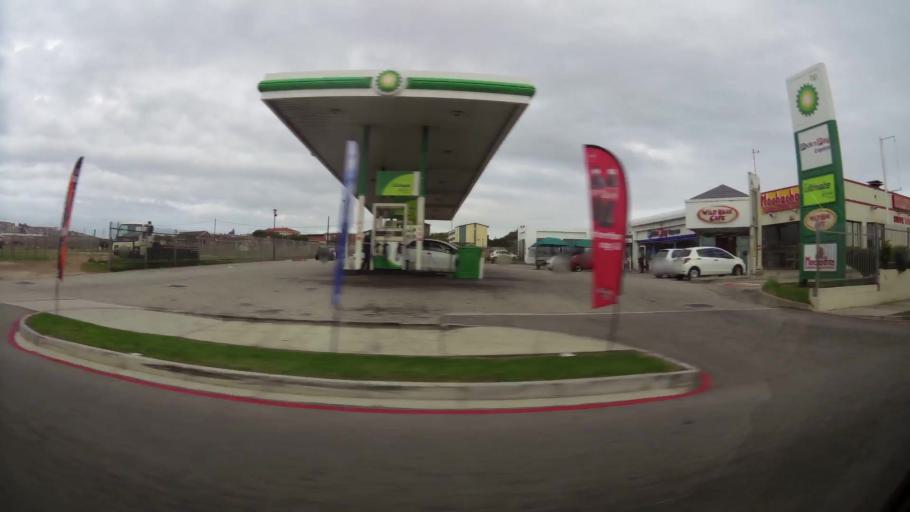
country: ZA
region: Eastern Cape
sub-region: Nelson Mandela Bay Metropolitan Municipality
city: Port Elizabeth
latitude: -33.9199
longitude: 25.5649
